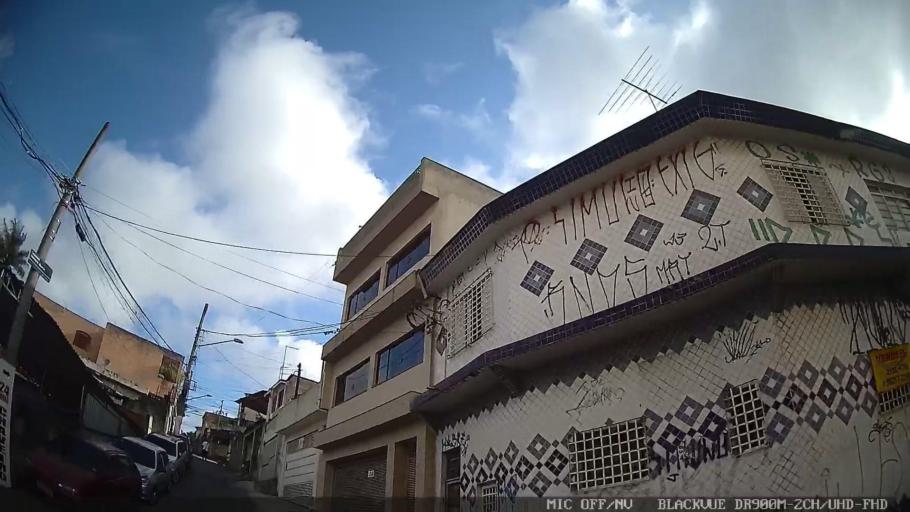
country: BR
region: Sao Paulo
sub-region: Sao Caetano Do Sul
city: Sao Caetano do Sul
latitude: -23.5774
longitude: -46.5256
